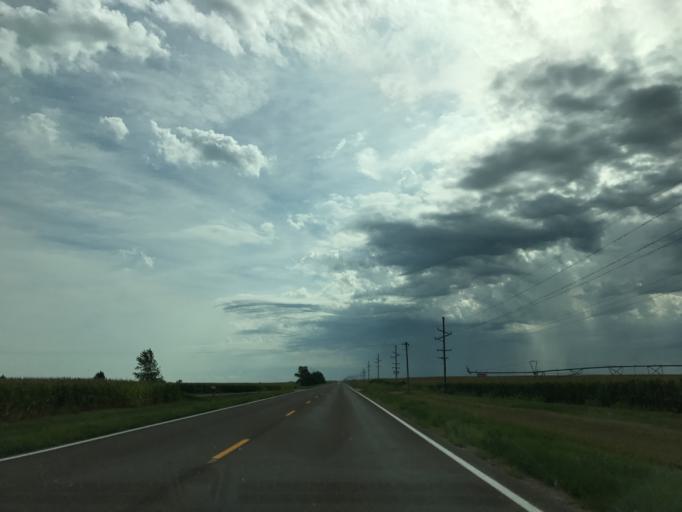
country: US
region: Nebraska
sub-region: Jefferson County
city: Fairbury
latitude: 40.3061
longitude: -97.0832
